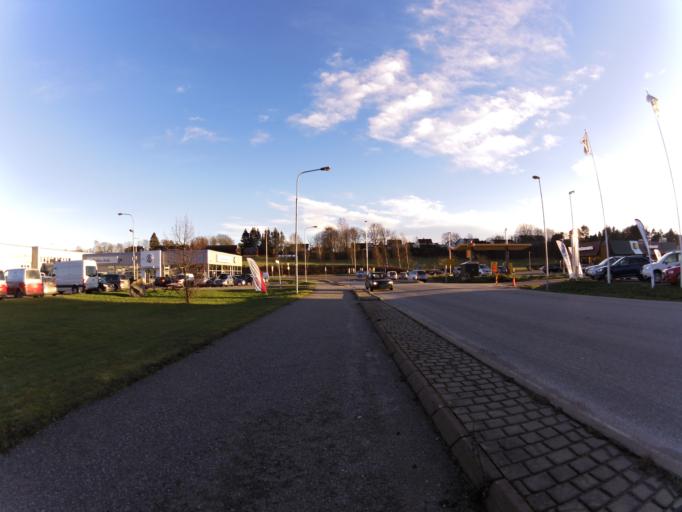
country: NO
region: Ostfold
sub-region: Fredrikstad
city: Fredrikstad
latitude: 59.2380
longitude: 10.9658
